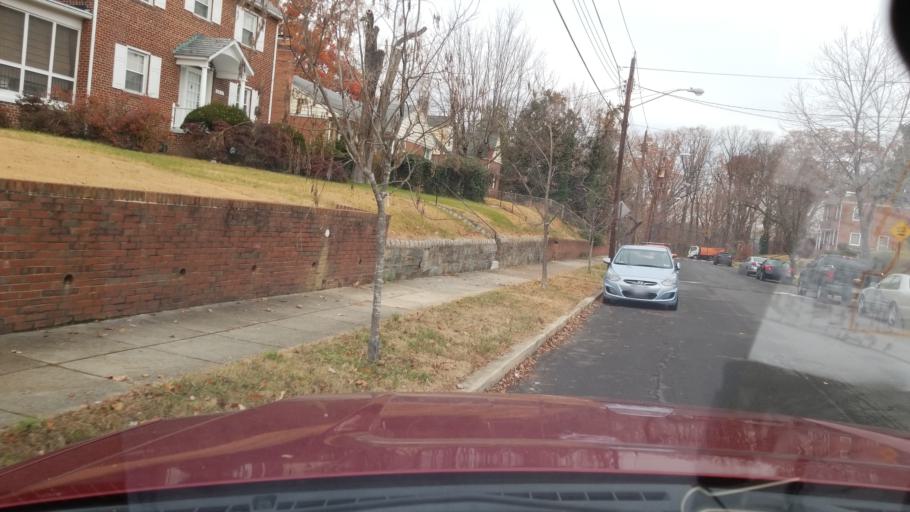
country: US
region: Maryland
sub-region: Prince George's County
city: Silver Hill
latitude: 38.8644
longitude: -76.9581
